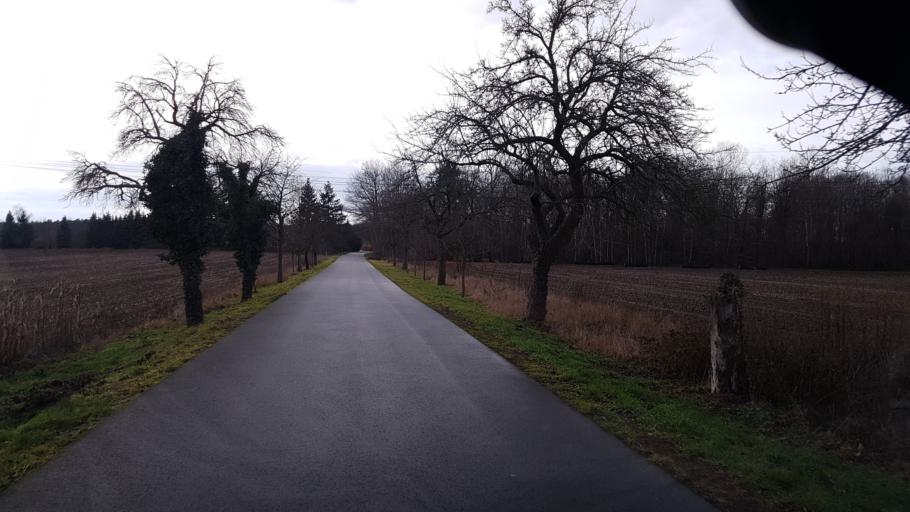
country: DE
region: Brandenburg
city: Altdobern
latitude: 51.6554
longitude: 14.0036
